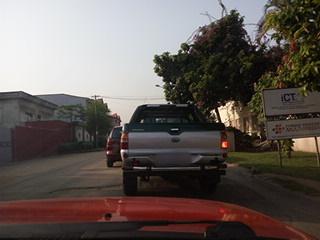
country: CI
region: Lagunes
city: Abobo
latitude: 5.3874
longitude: -3.9918
